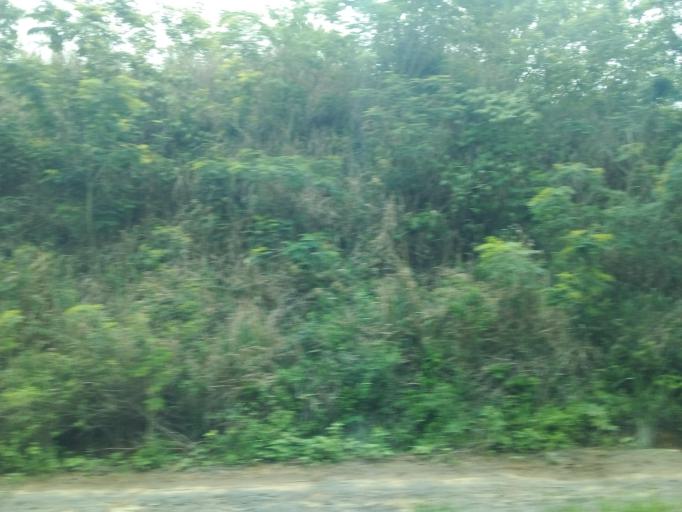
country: BR
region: Minas Gerais
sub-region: Governador Valadares
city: Governador Valadares
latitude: -19.0895
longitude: -42.1633
